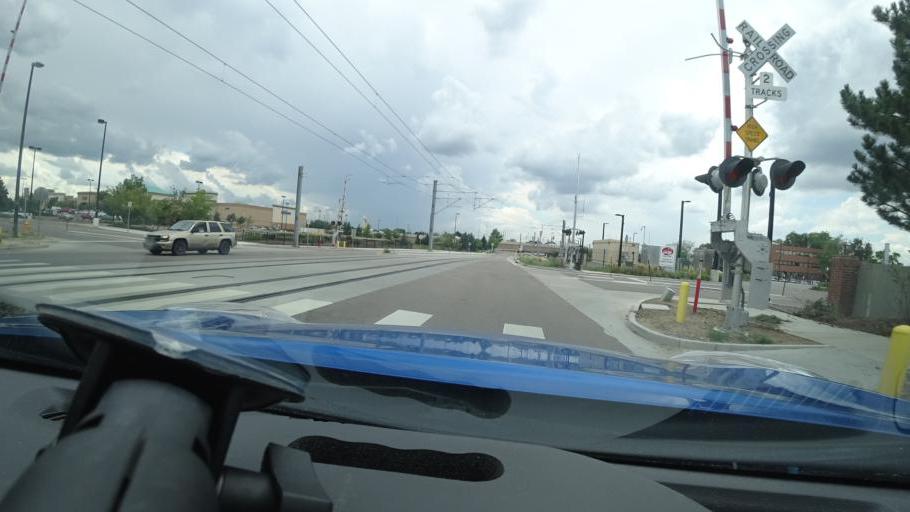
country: US
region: Colorado
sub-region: Adams County
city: Aurora
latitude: 39.7166
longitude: -104.8238
